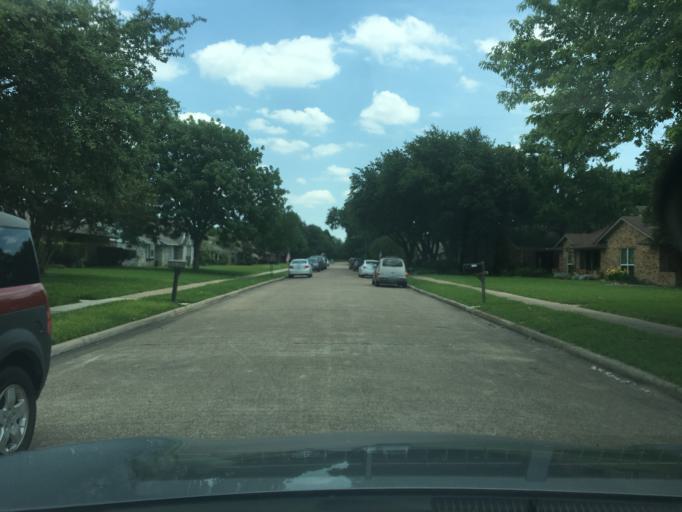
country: US
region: Texas
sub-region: Dallas County
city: Richardson
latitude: 32.9600
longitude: -96.6900
